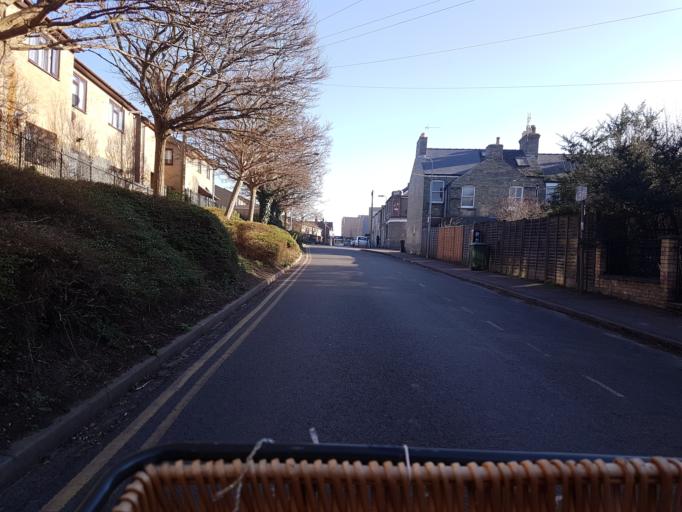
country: GB
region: England
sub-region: Cambridgeshire
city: Cambridge
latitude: 52.2109
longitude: 0.1416
